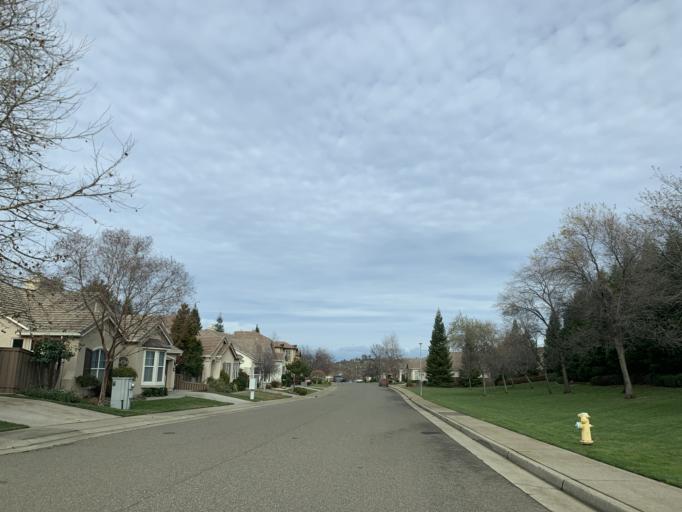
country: US
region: California
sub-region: El Dorado County
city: El Dorado Hills
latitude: 38.6804
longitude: -121.1018
